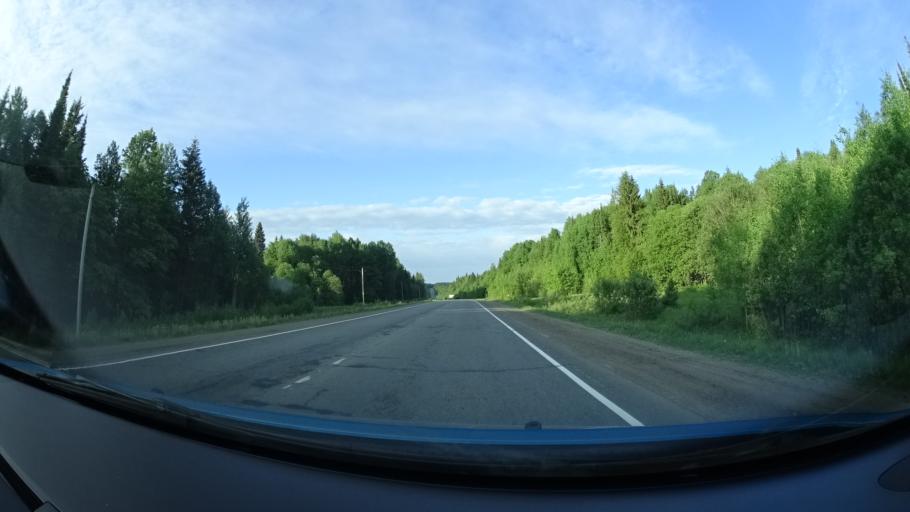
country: RU
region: Perm
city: Kultayevo
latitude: 57.8064
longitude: 55.7855
